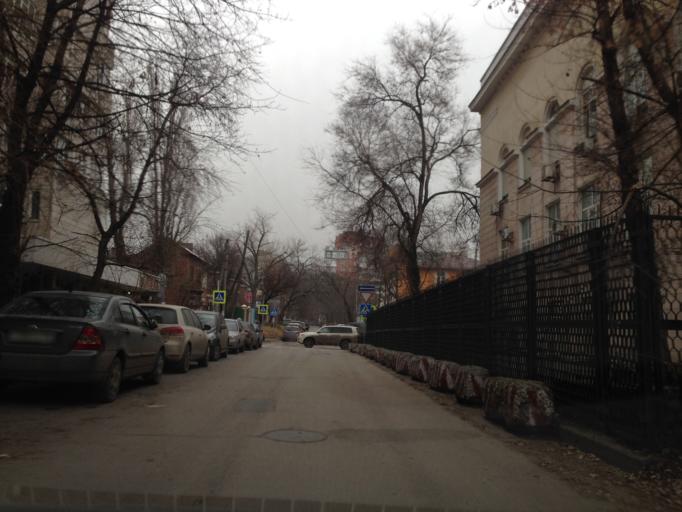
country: RU
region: Rostov
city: Rostov-na-Donu
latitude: 47.2304
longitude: 39.7083
